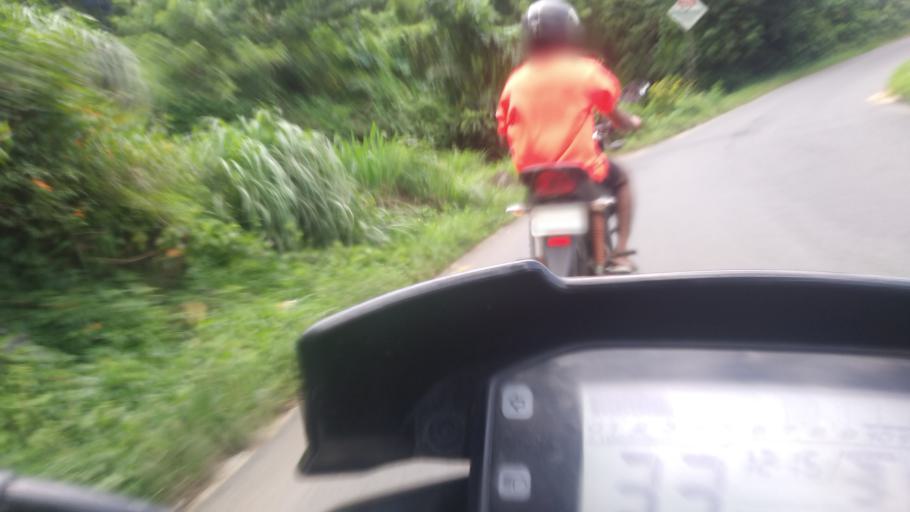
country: IN
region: Kerala
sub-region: Idukki
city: Munnar
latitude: 10.0131
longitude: 77.0071
